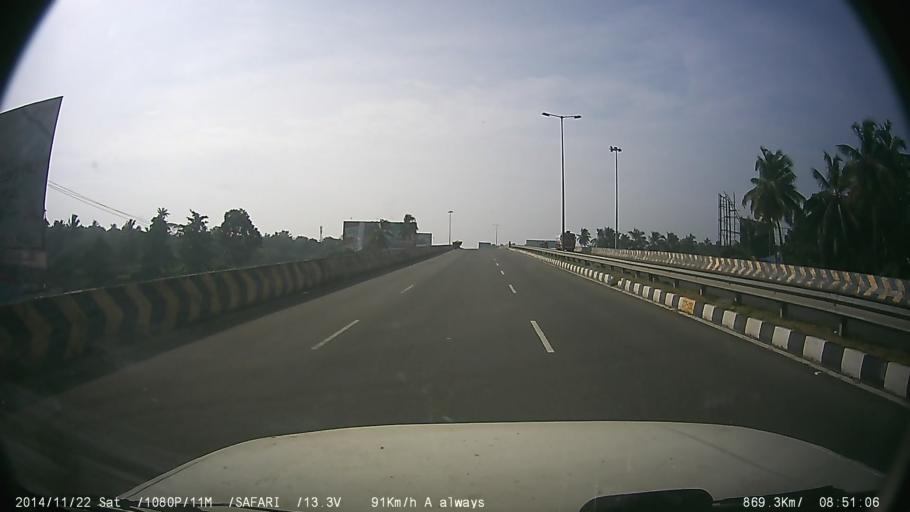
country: IN
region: Kerala
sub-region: Thrissur District
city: Trichur
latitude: 10.4521
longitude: 76.2582
